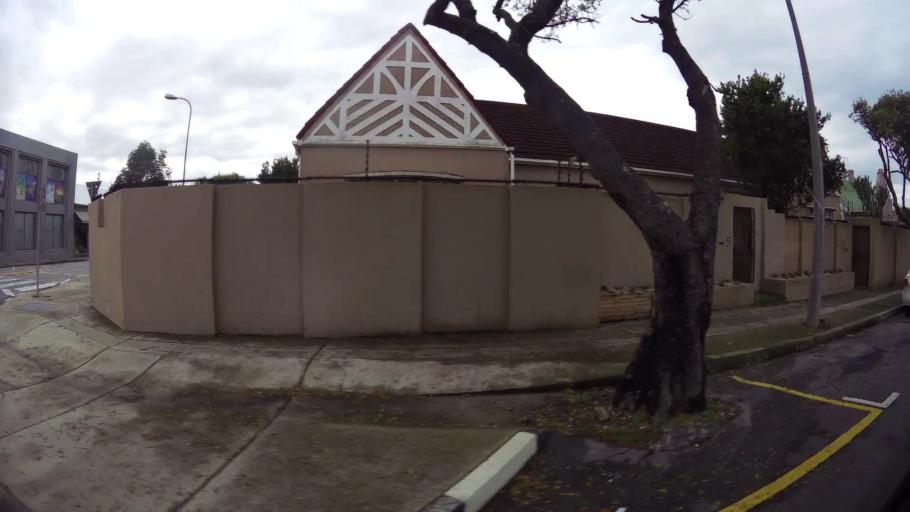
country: ZA
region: Eastern Cape
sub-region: Nelson Mandela Bay Metropolitan Municipality
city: Port Elizabeth
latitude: -33.9606
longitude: 25.6054
